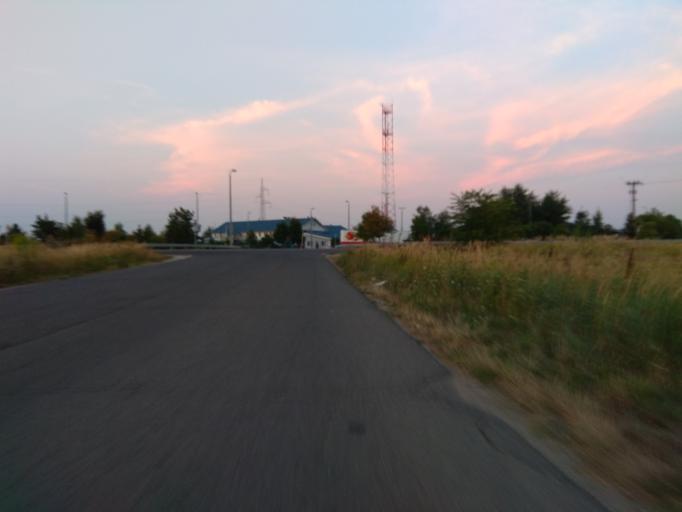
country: HU
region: Borsod-Abauj-Zemplen
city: Emod
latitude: 47.9231
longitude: 20.8400
